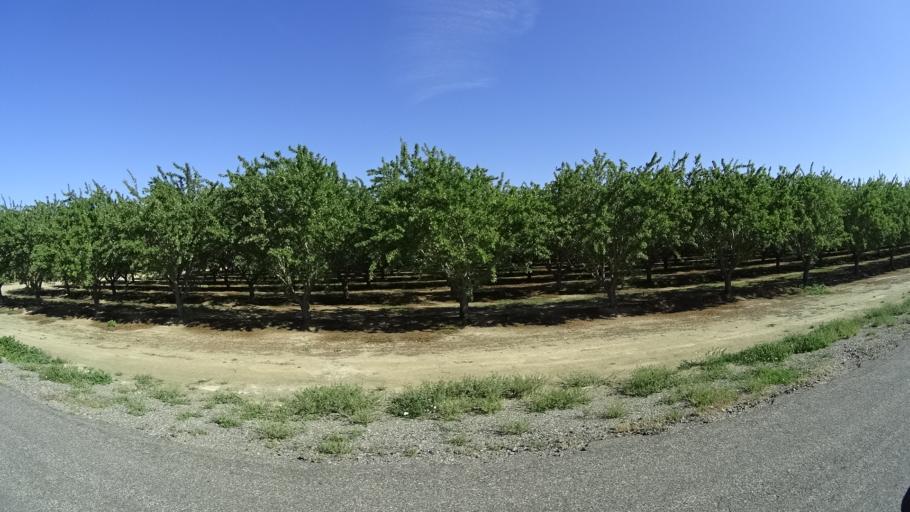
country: US
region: California
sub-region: Glenn County
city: Willows
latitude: 39.6112
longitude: -122.1673
